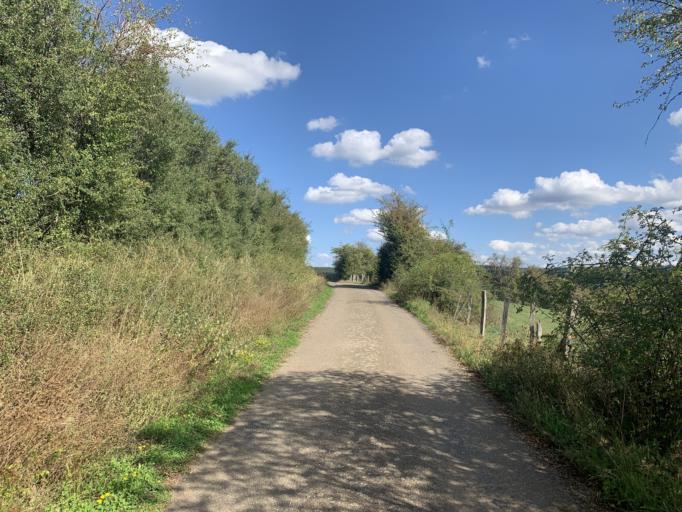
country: BE
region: Wallonia
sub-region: Province du Luxembourg
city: Tellin
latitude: 50.0975
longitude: 5.2762
